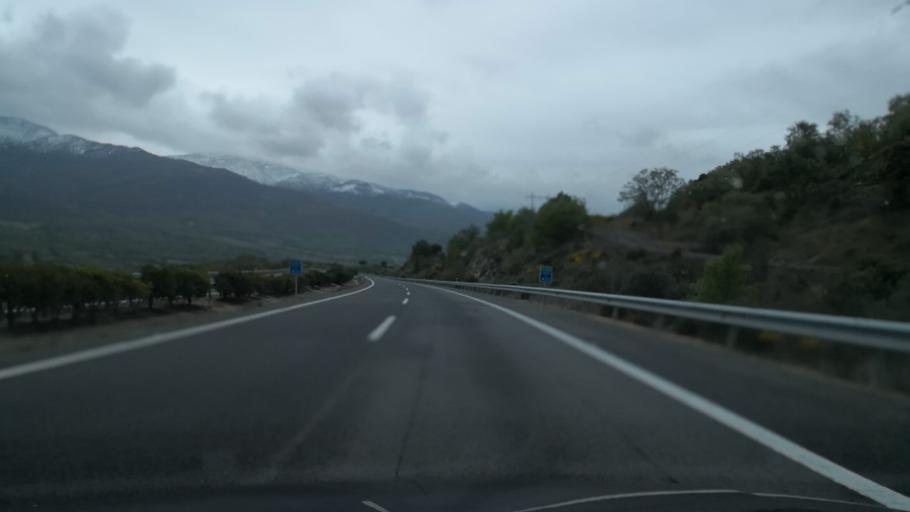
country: ES
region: Extremadura
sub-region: Provincia de Caceres
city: Hervas
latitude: 40.2887
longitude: -5.8997
